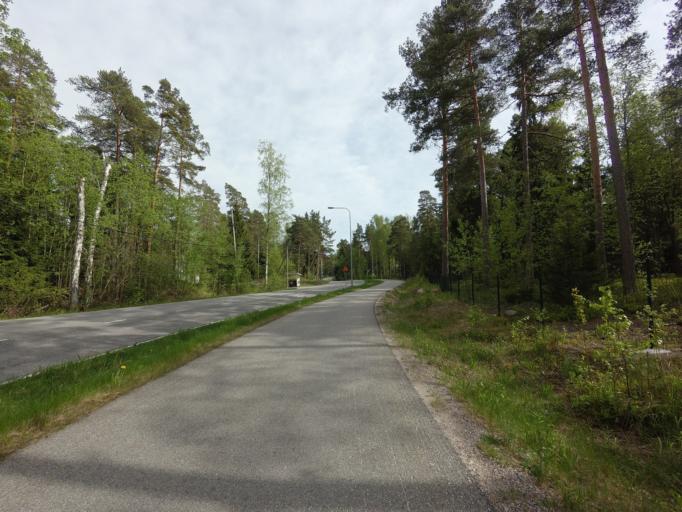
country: FI
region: Uusimaa
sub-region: Helsinki
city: Koukkuniemi
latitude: 60.1256
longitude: 24.7127
